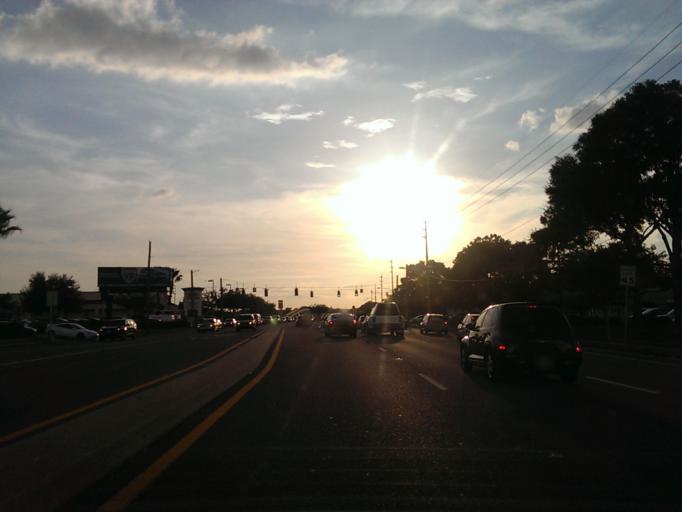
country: US
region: Florida
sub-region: Orange County
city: Tangelo Park
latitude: 28.4940
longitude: -81.4597
